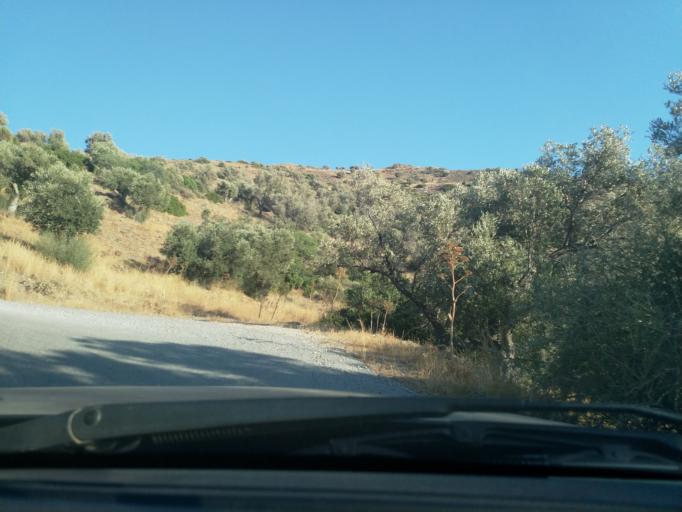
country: GR
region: Crete
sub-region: Nomos Rethymnis
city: Agia Galini
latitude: 35.1119
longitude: 24.5653
